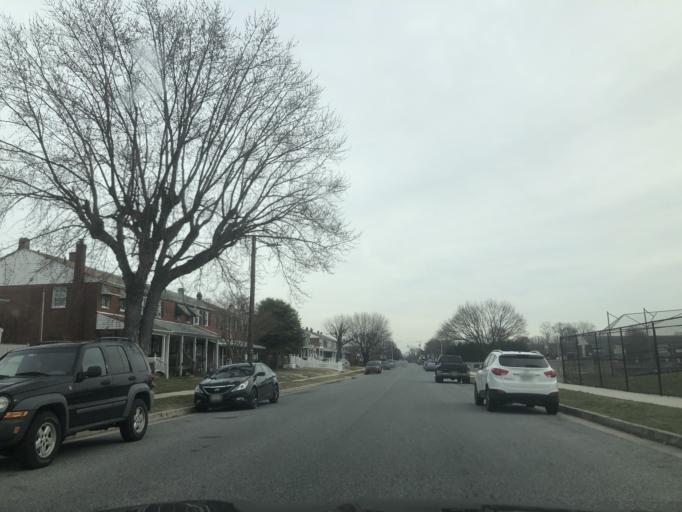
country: US
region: Maryland
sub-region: Baltimore County
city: Dundalk
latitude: 39.2679
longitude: -76.4873
